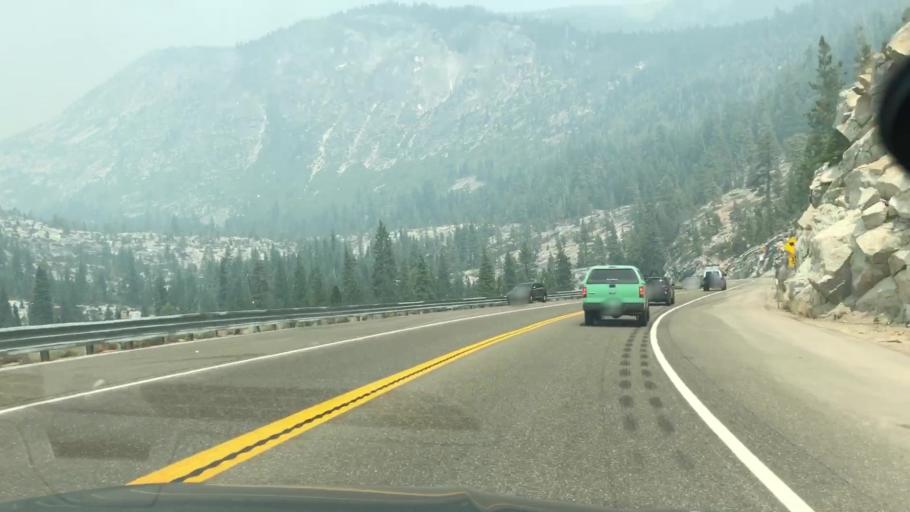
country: US
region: California
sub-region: El Dorado County
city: South Lake Tahoe
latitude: 38.8077
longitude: -120.1229
